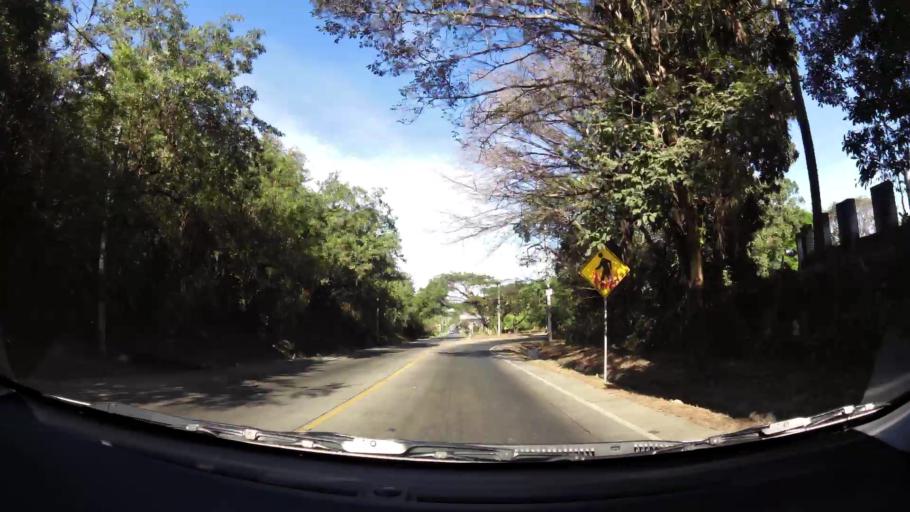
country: SV
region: Santa Ana
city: Santa Ana
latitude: 14.0110
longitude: -89.5440
